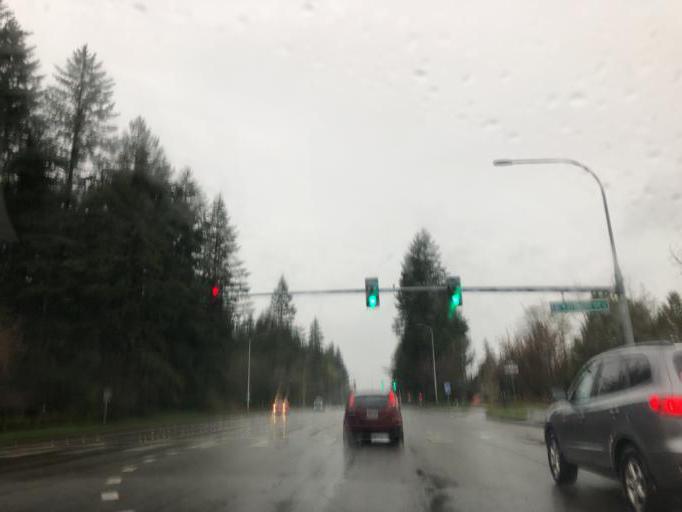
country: US
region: Washington
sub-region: Thurston County
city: Lacey
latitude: 47.0495
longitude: -122.8097
